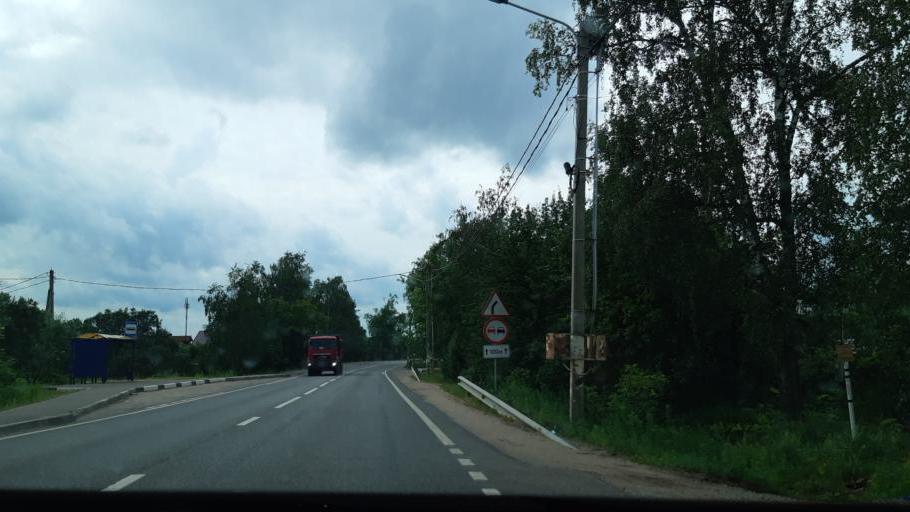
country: RU
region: Moskovskaya
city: Dorokhovo
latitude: 55.5400
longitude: 36.3611
